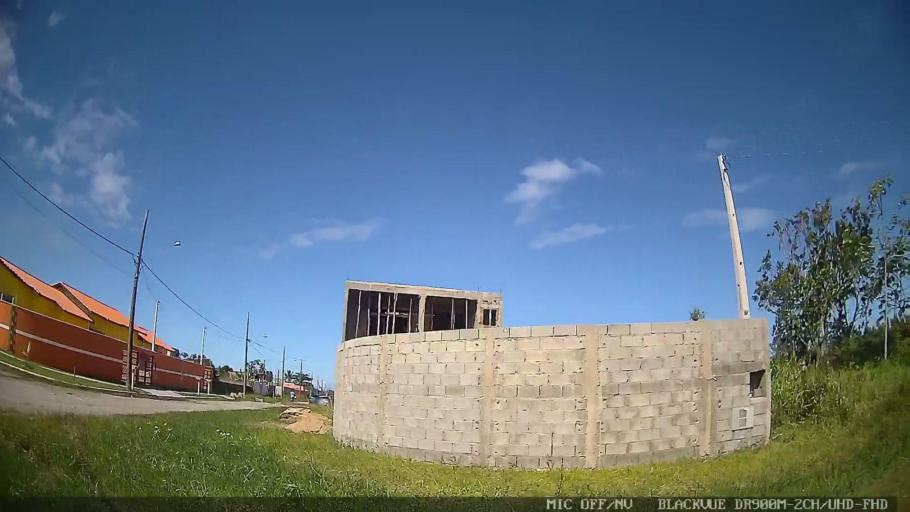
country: BR
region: Sao Paulo
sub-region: Itanhaem
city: Itanhaem
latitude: -24.2245
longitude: -46.8830
